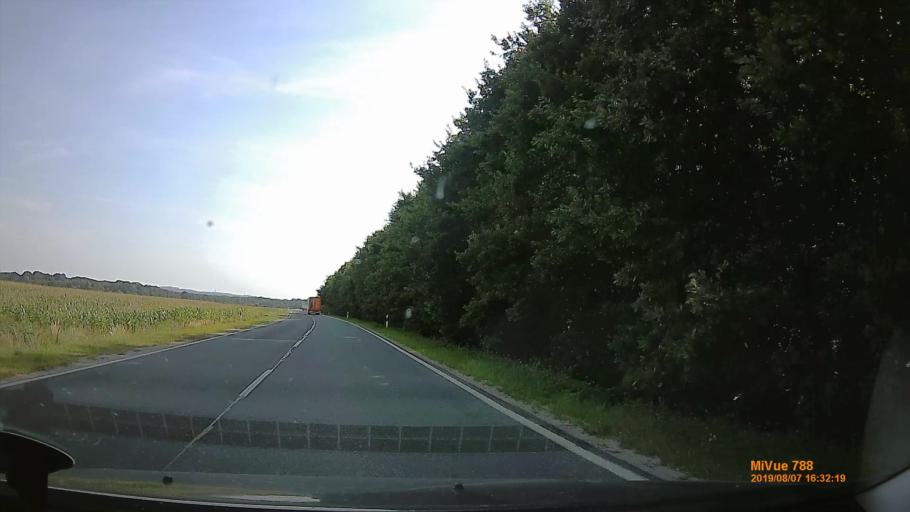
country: HU
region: Zala
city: Lenti
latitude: 46.6481
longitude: 16.4916
